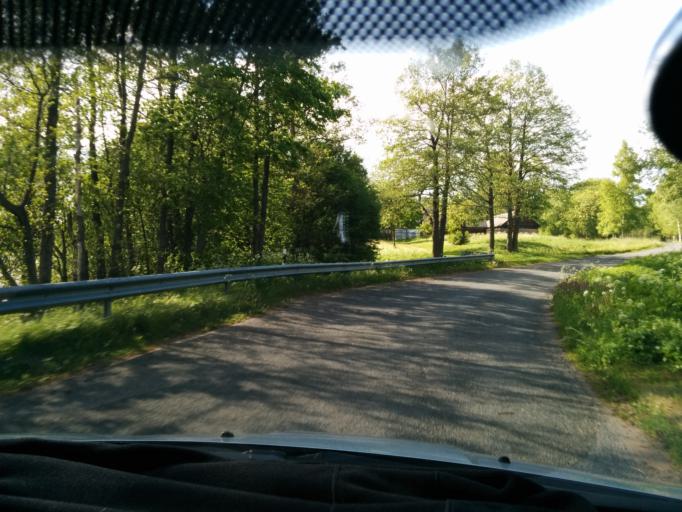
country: EE
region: Harju
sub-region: Loksa linn
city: Loksa
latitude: 59.6121
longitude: 25.6986
